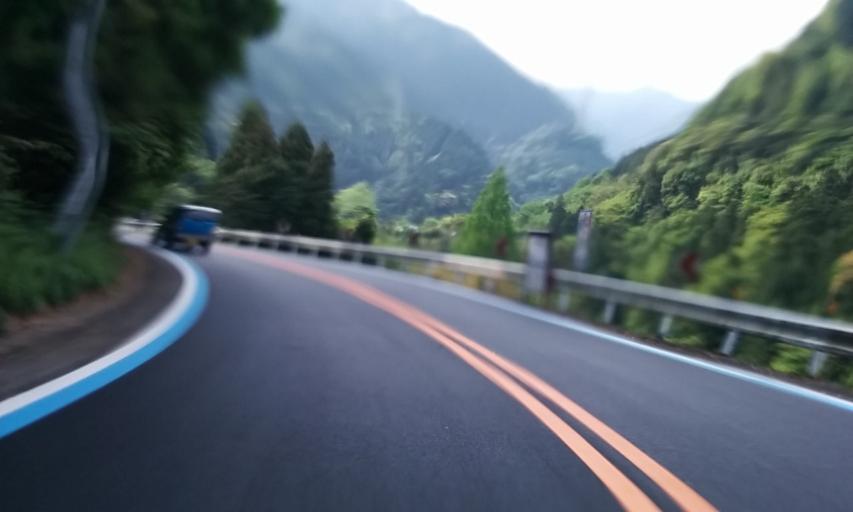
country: JP
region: Ehime
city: Niihama
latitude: 33.9056
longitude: 133.3086
